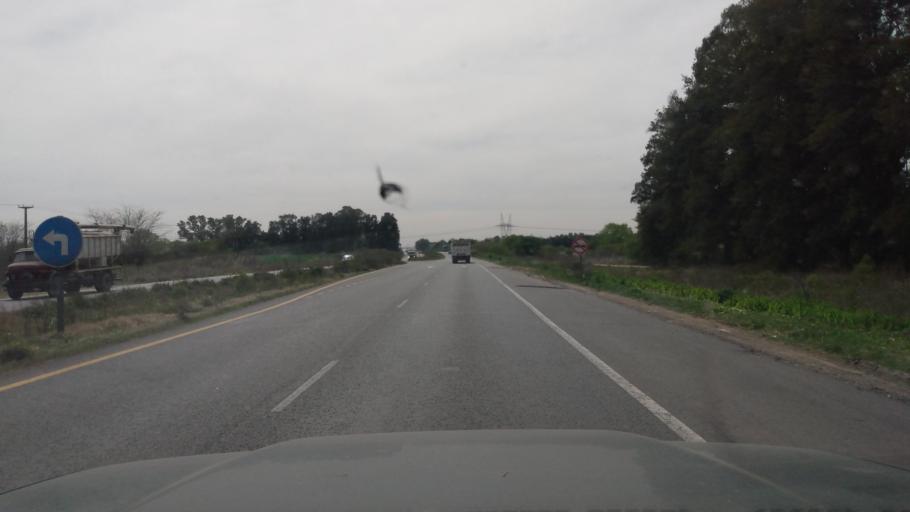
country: AR
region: Buenos Aires
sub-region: Partido de Lujan
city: Lujan
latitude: -34.4565
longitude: -59.0578
